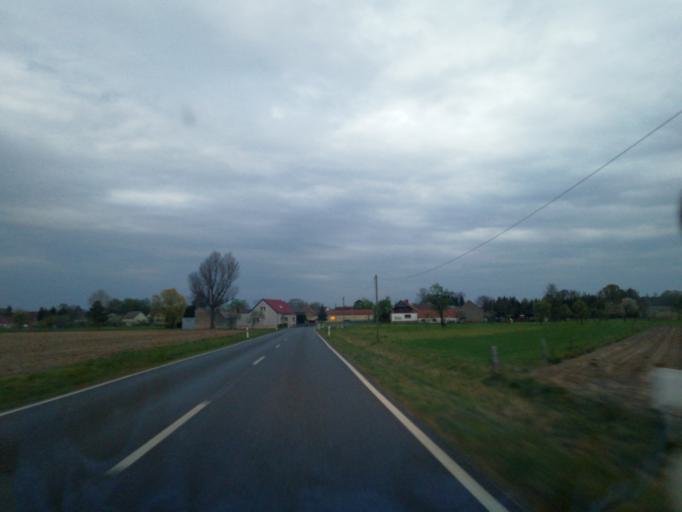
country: DE
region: Brandenburg
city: Calau
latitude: 51.7638
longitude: 13.9074
